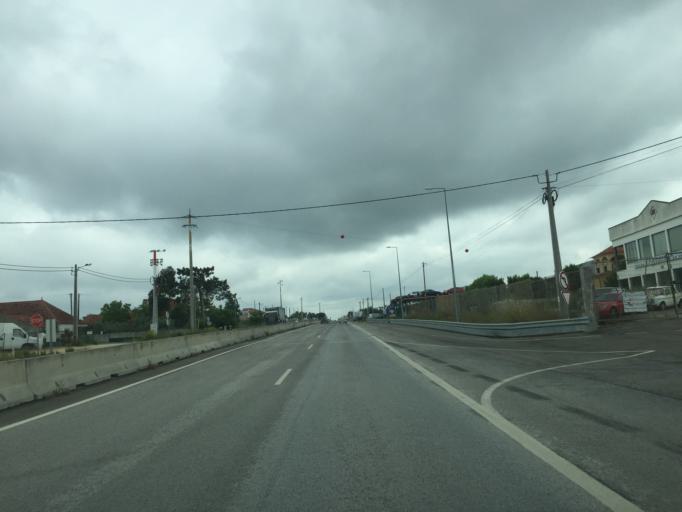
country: PT
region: Leiria
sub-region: Alcobaca
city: Aljubarrota
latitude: 39.5594
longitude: -8.8859
